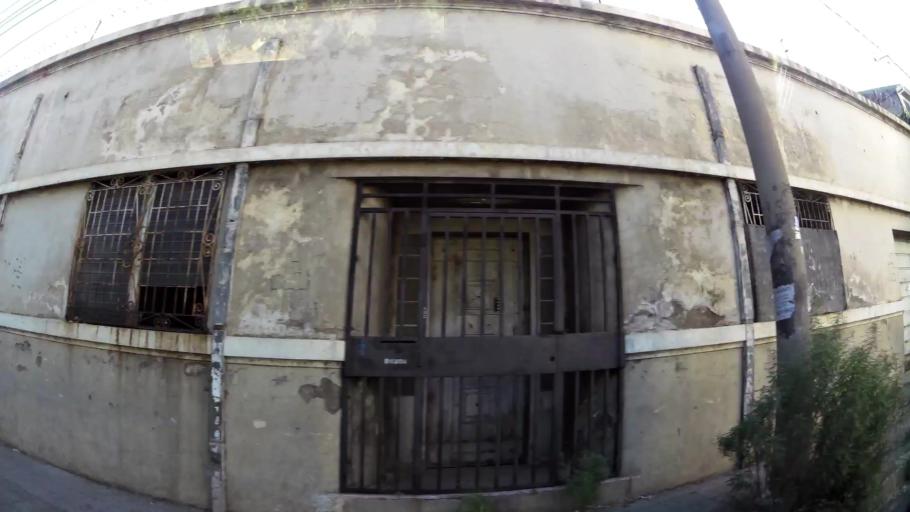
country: SV
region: Santa Ana
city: Santa Ana
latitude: 13.9942
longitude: -89.5612
